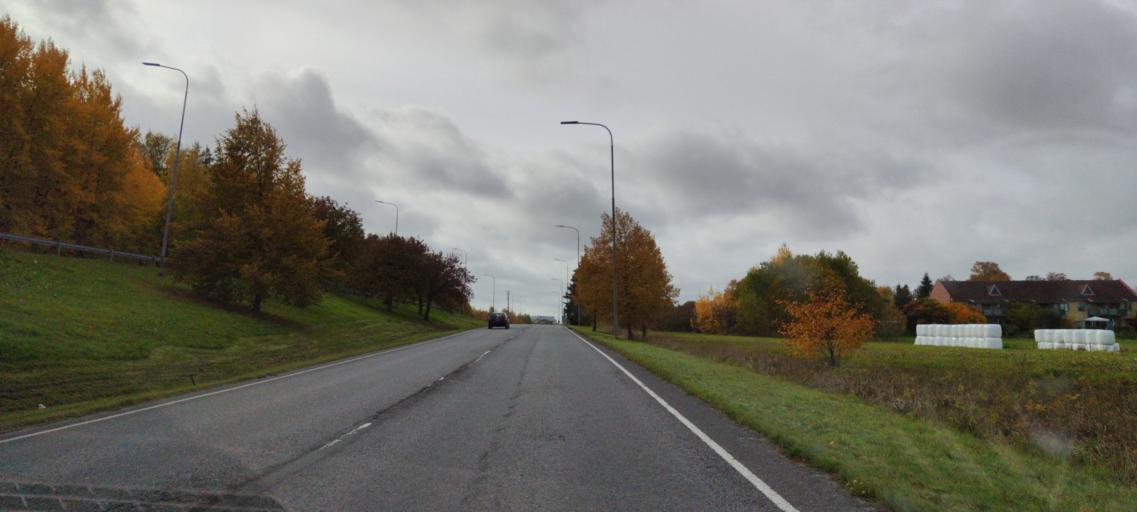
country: FI
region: Varsinais-Suomi
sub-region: Turku
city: Turku
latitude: 60.4610
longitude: 22.3157
